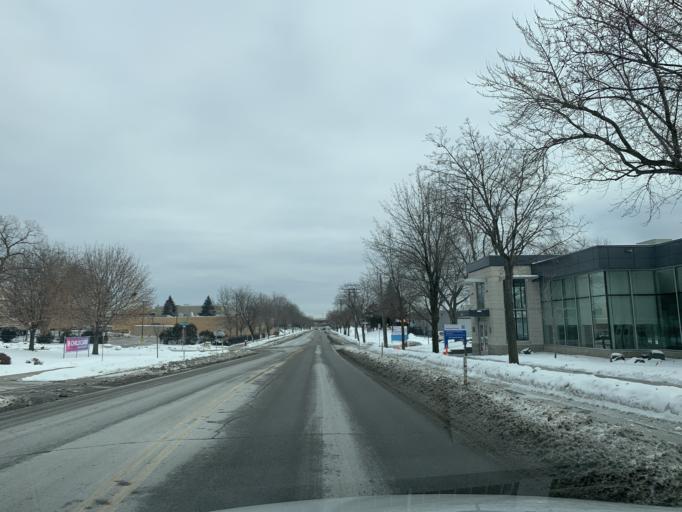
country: US
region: Minnesota
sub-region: Hennepin County
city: Minneapolis
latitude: 44.9921
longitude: -93.2936
